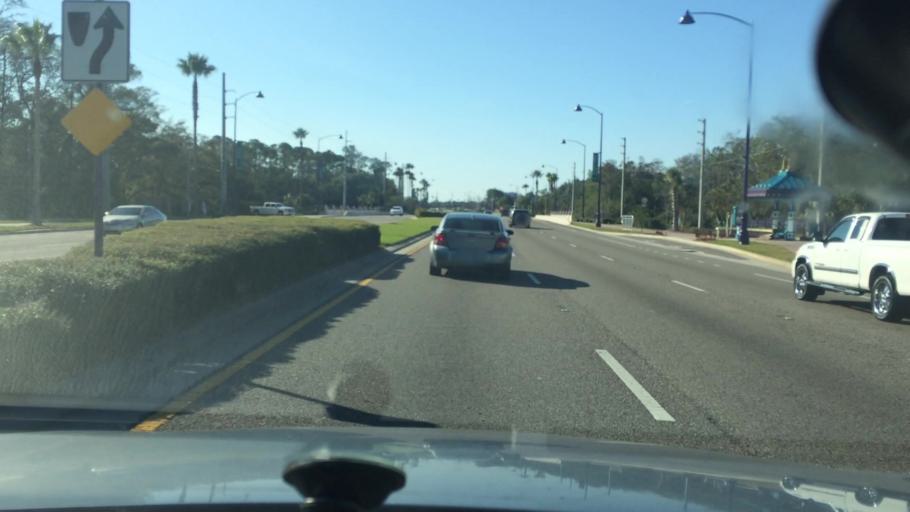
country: US
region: Florida
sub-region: Osceola County
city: Kissimmee
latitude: 28.3044
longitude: -81.4495
